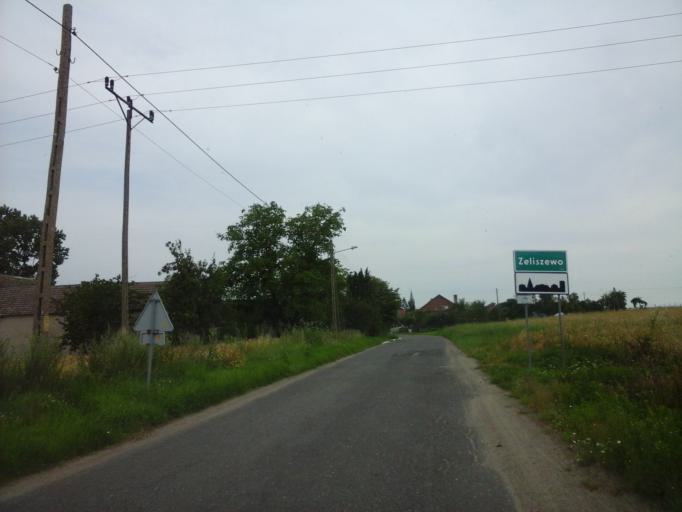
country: PL
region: West Pomeranian Voivodeship
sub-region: Powiat choszczenski
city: Recz
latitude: 53.2107
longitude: 15.5472
